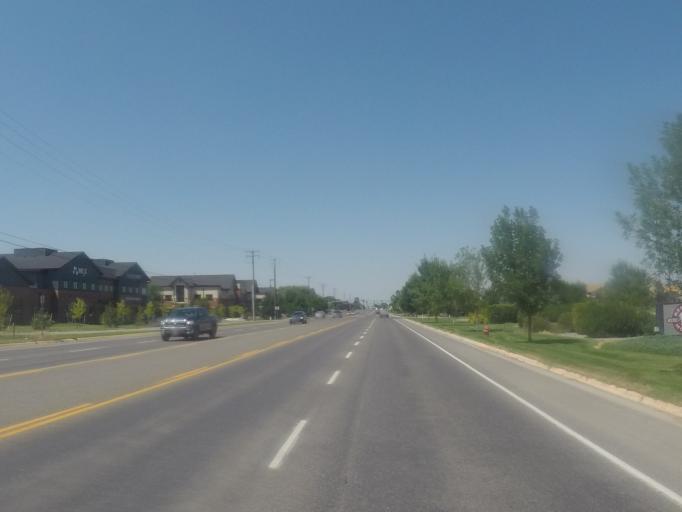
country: US
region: Montana
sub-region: Gallatin County
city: Bozeman
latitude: 45.6931
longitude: -111.0533
